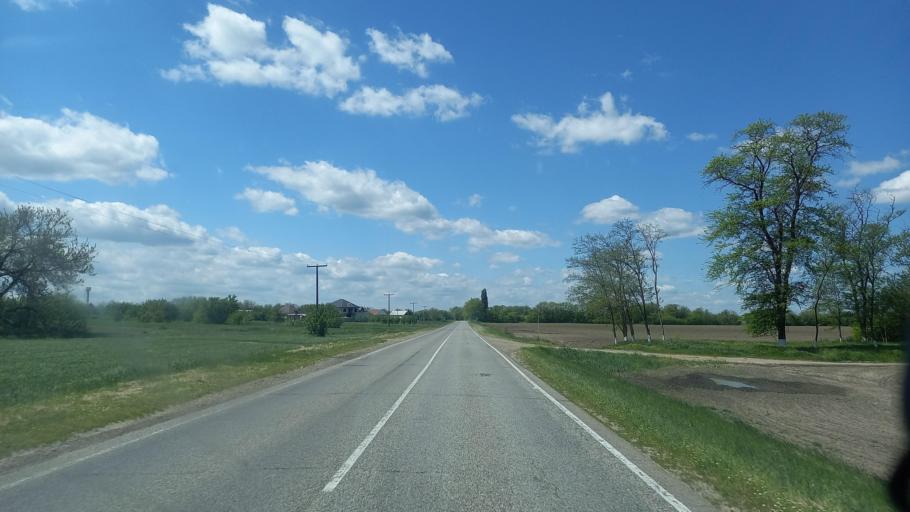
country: RU
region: Krasnodarskiy
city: Kazanskaya
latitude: 45.3443
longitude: 40.3281
